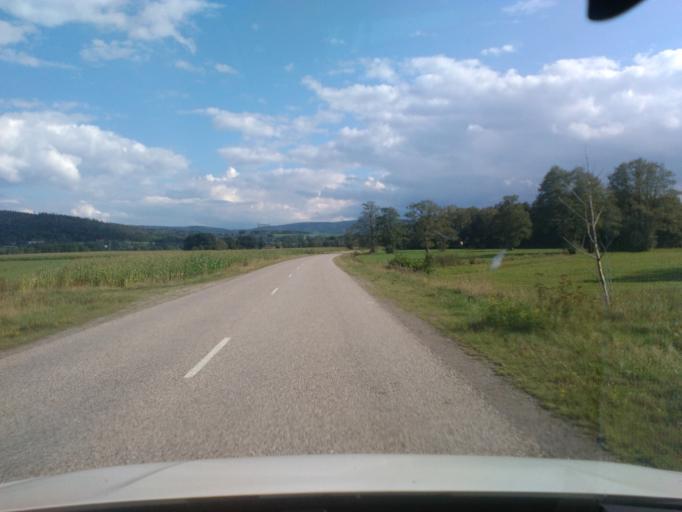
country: FR
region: Lorraine
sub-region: Departement des Vosges
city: Corcieux
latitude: 48.1957
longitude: 6.8796
